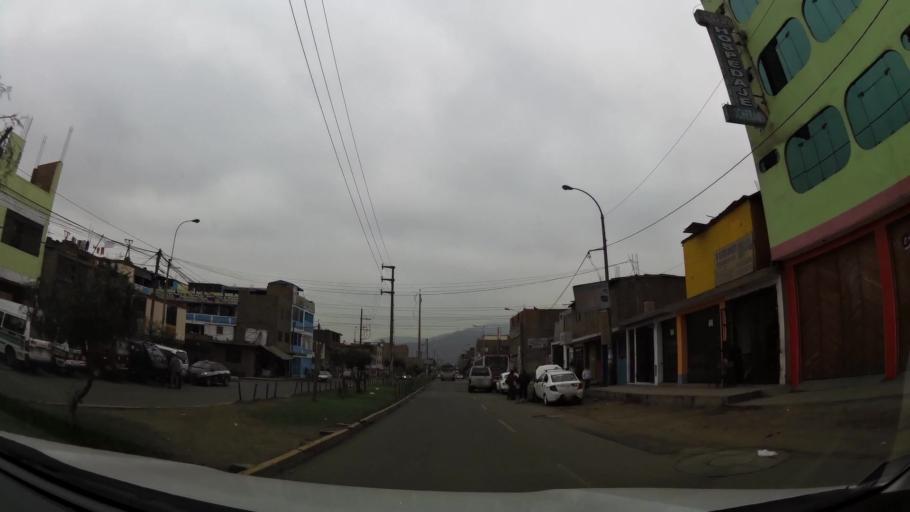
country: PE
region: Lima
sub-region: Lima
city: Vitarte
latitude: -12.0379
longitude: -76.9624
